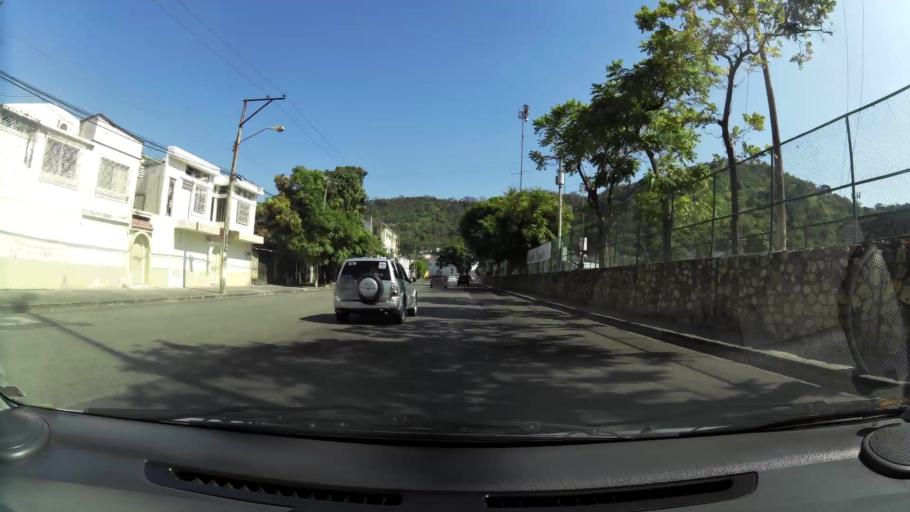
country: EC
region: Guayas
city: Guayaquil
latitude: -2.1642
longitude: -79.9216
